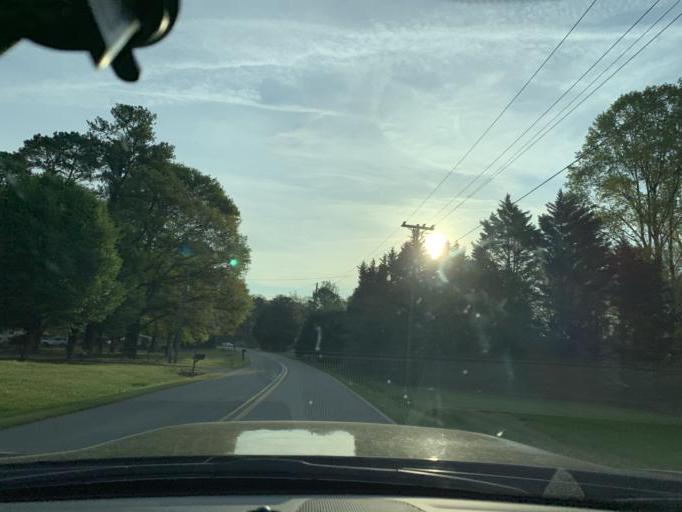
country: US
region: Georgia
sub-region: Forsyth County
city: Cumming
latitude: 34.2590
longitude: -84.1547
